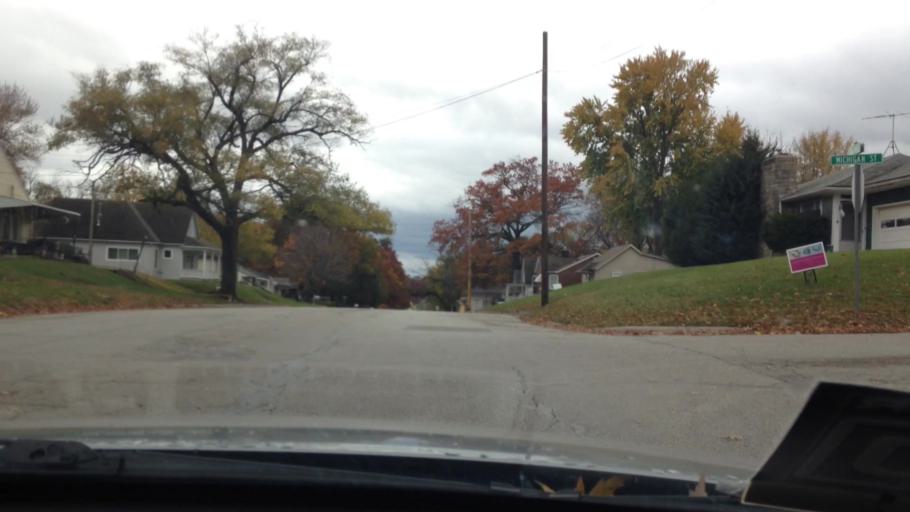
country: US
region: Kansas
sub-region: Leavenworth County
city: Leavenworth
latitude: 39.3021
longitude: -94.9136
